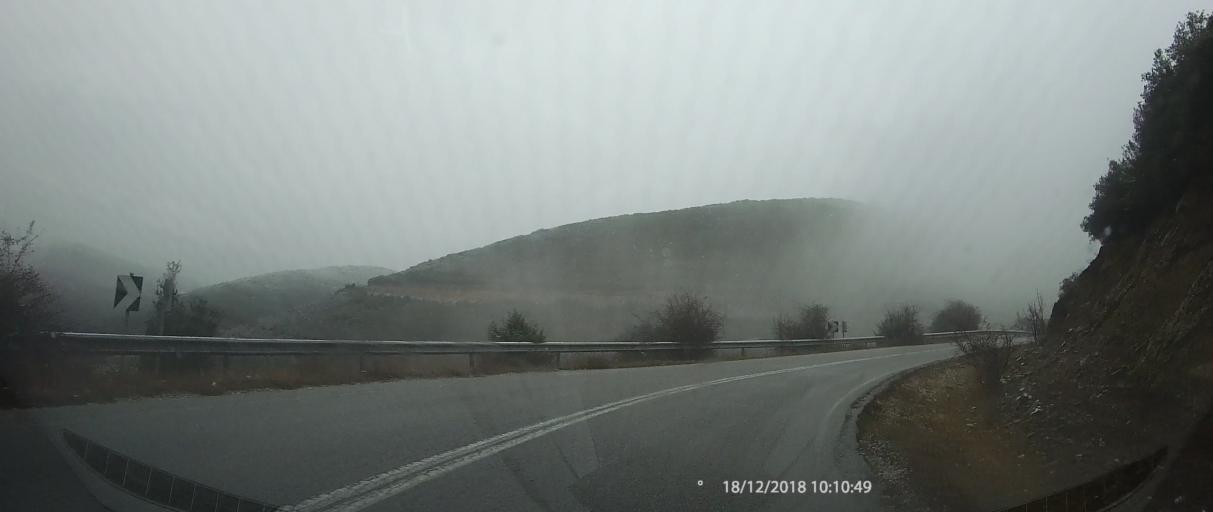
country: GR
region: Thessaly
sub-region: Nomos Larisis
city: Livadi
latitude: 40.0900
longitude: 22.2095
